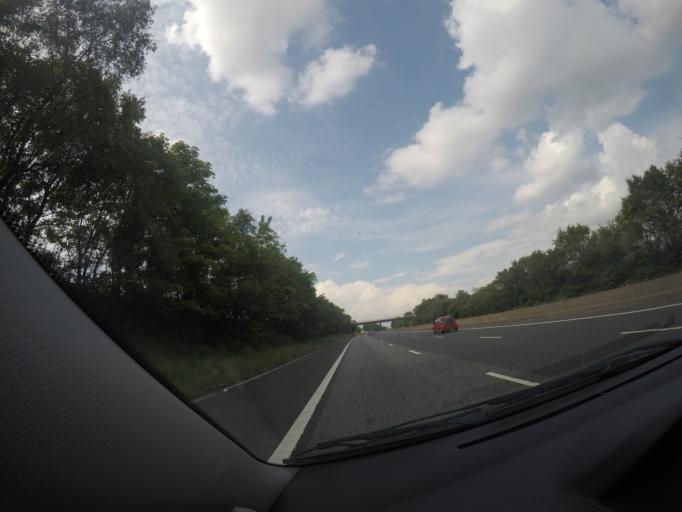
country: GB
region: England
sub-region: Cumbria
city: Scotby
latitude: 54.8244
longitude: -2.8890
